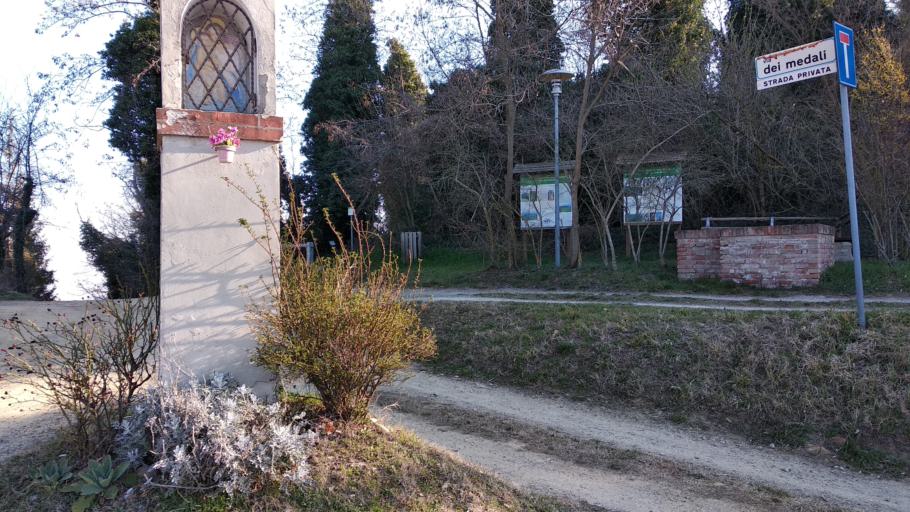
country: IT
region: Emilia-Romagna
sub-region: Provincia di Bologna
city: Ozzano dell'Emilia
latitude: 44.3960
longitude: 11.4616
